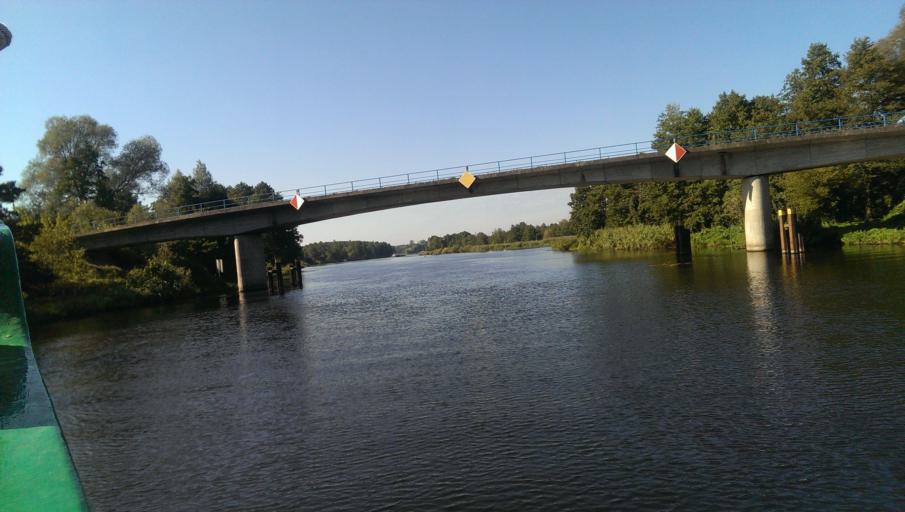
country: DE
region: Brandenburg
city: Liepe
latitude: 52.8582
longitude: 13.9727
